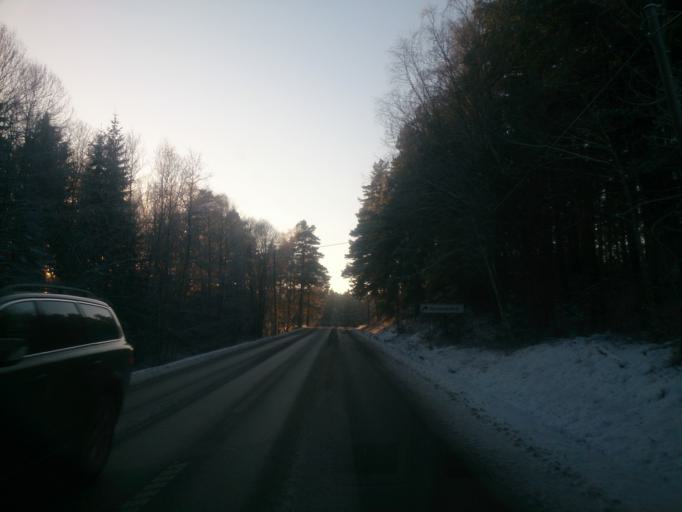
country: SE
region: OEstergoetland
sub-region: Norrkopings Kommun
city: Norrkoping
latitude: 58.4901
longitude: 16.1130
